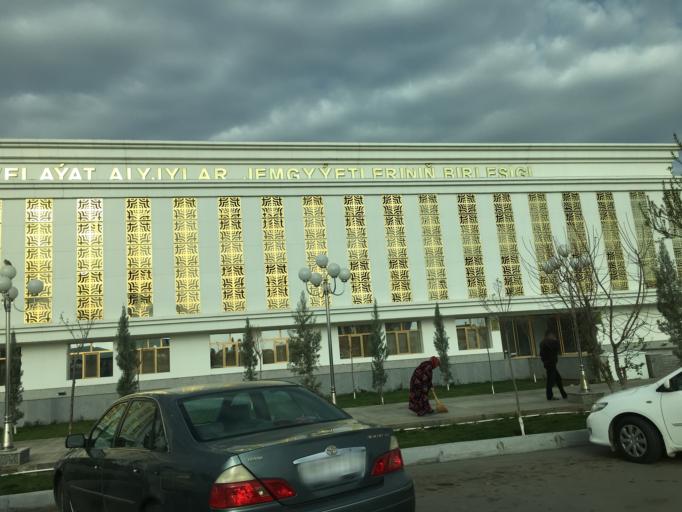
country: TM
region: Lebap
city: Turkmenabat
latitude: 39.0771
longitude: 63.5864
